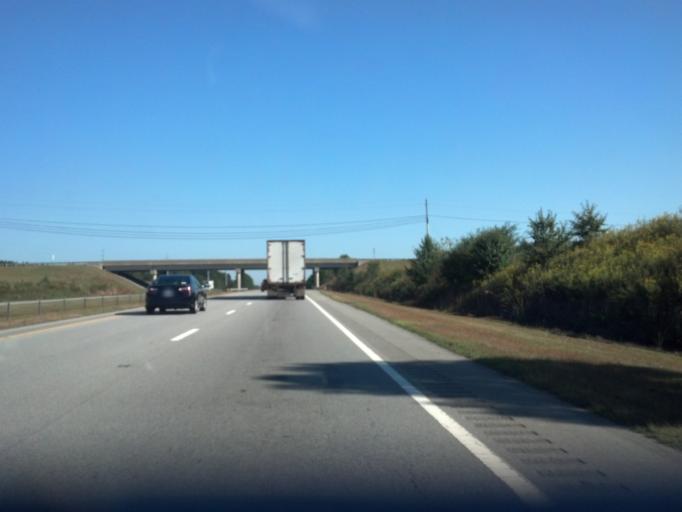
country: US
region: North Carolina
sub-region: Pitt County
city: Summerfield
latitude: 35.6275
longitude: -77.4343
